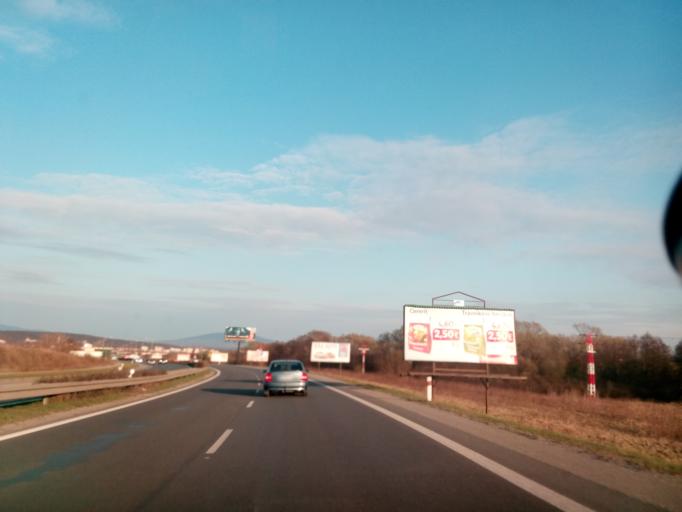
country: SK
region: Kosicky
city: Kosice
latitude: 48.6886
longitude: 21.2484
